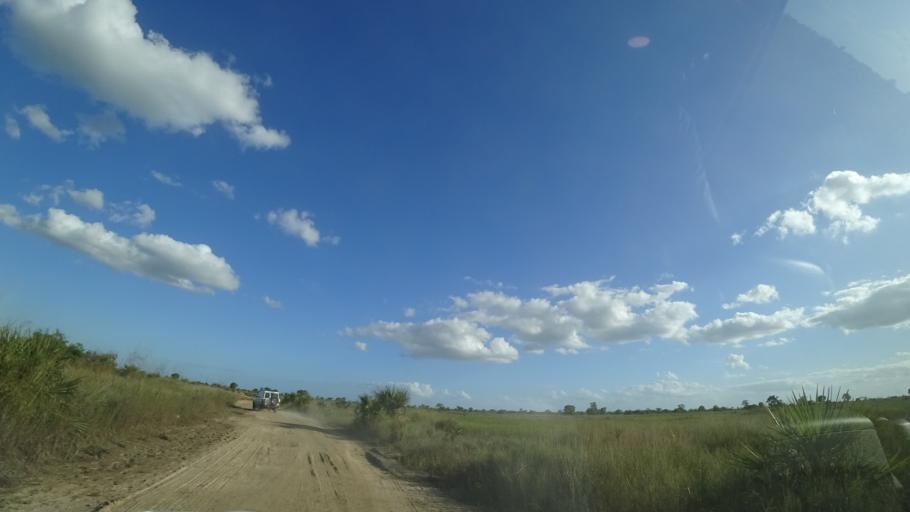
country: MZ
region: Sofala
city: Dondo
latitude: -19.4085
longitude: 34.5661
